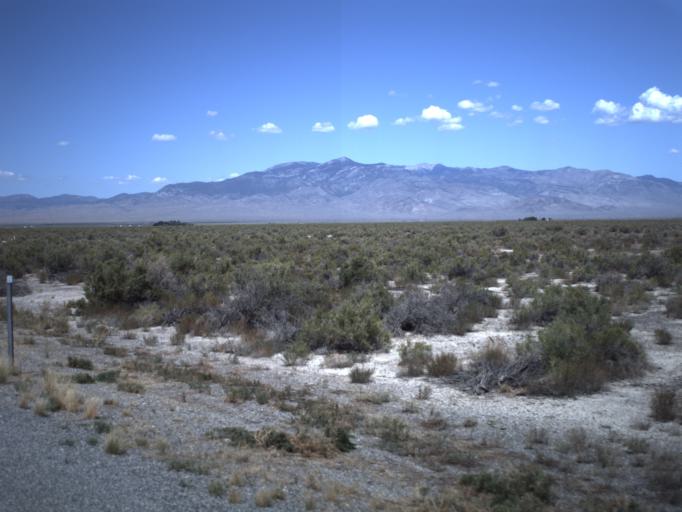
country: US
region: Nevada
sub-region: White Pine County
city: McGill
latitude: 39.0490
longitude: -113.9419
